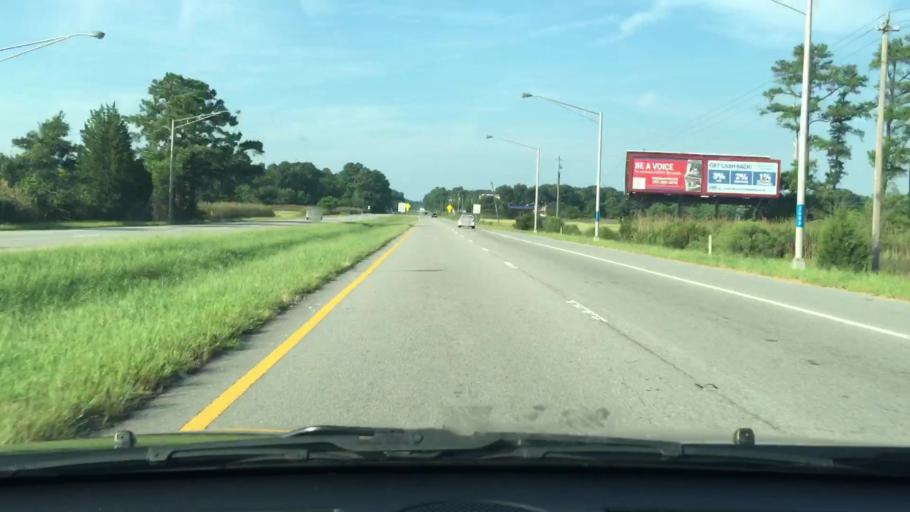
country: US
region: Virginia
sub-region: Isle of Wight County
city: Carrollton
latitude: 36.9669
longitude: -76.5129
